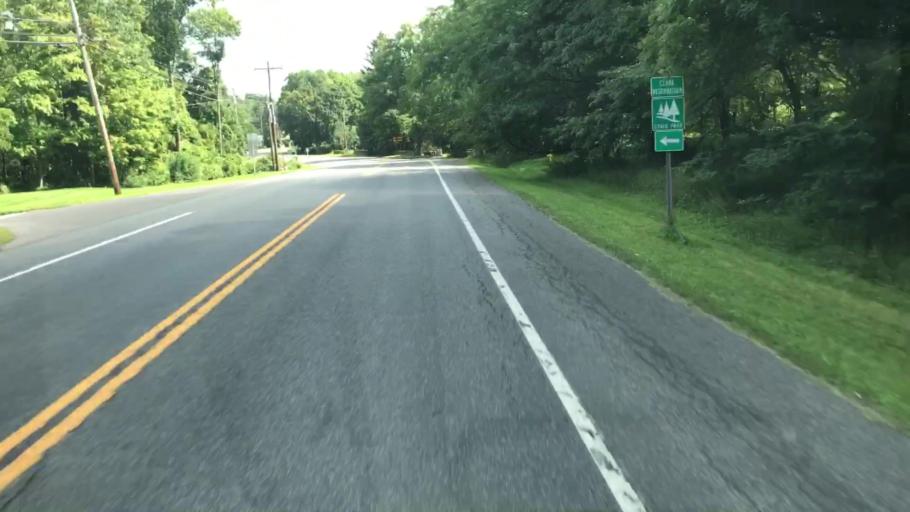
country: US
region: New York
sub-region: Onondaga County
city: Nedrow
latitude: 42.9930
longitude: -76.0951
